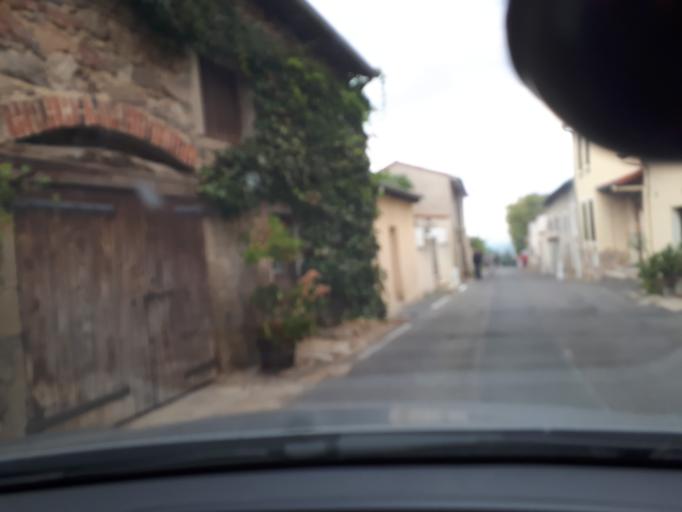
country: FR
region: Rhone-Alpes
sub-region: Departement de la Loire
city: Montbrison
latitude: 45.5916
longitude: 4.0504
